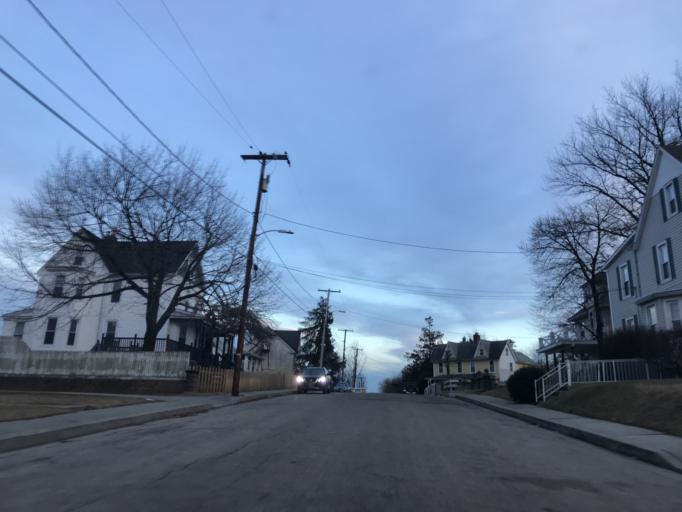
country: US
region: Maryland
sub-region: Baltimore County
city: Overlea
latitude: 39.3424
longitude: -76.5438
